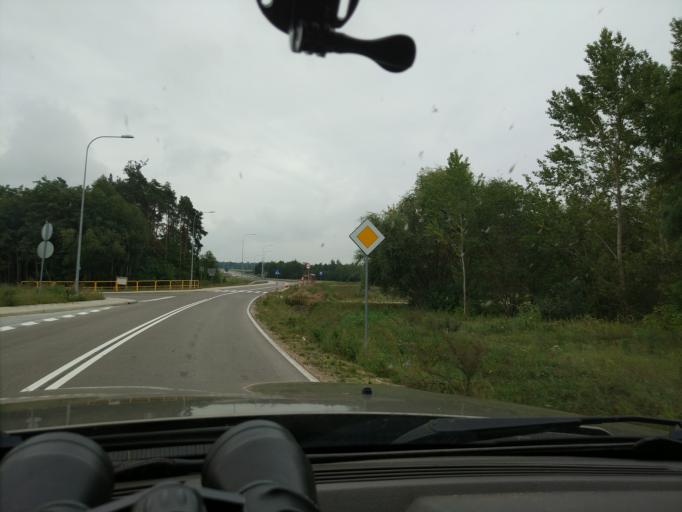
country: PL
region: Podlasie
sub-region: Powiat zambrowski
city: Szumowo
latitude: 52.9153
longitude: 22.0911
